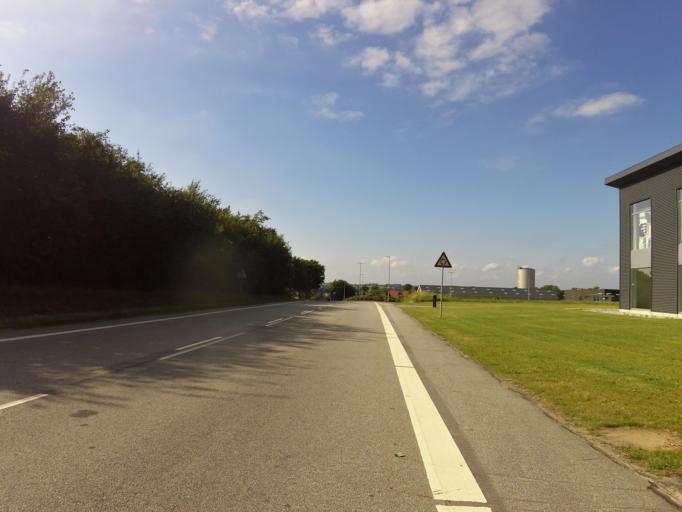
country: DK
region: South Denmark
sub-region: Vejen Kommune
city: Rodding
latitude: 55.3739
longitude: 9.0579
